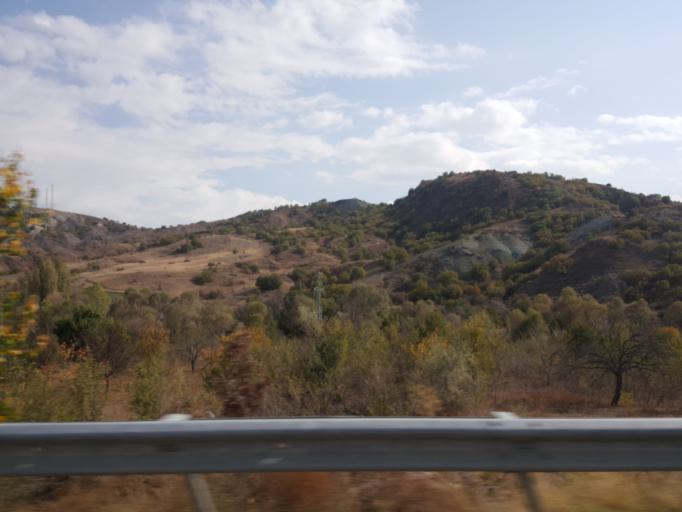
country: TR
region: Corum
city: Sungurlu
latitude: 40.1984
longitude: 34.5122
